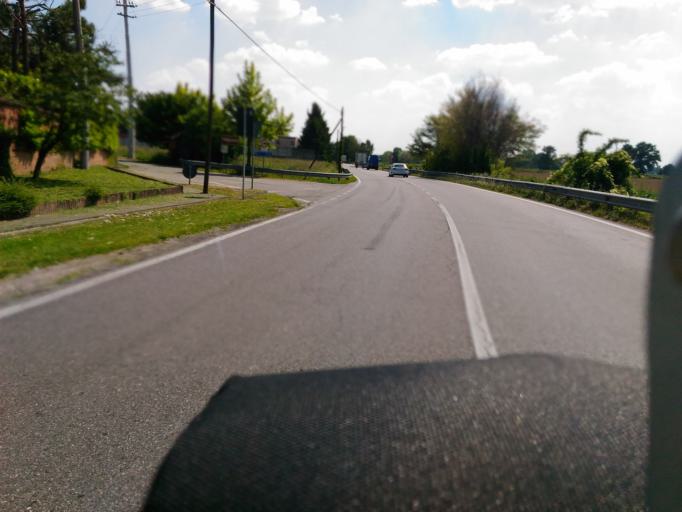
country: IT
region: Lombardy
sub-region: Citta metropolitana di Milano
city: Mombretto
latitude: 45.4105
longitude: 9.3589
